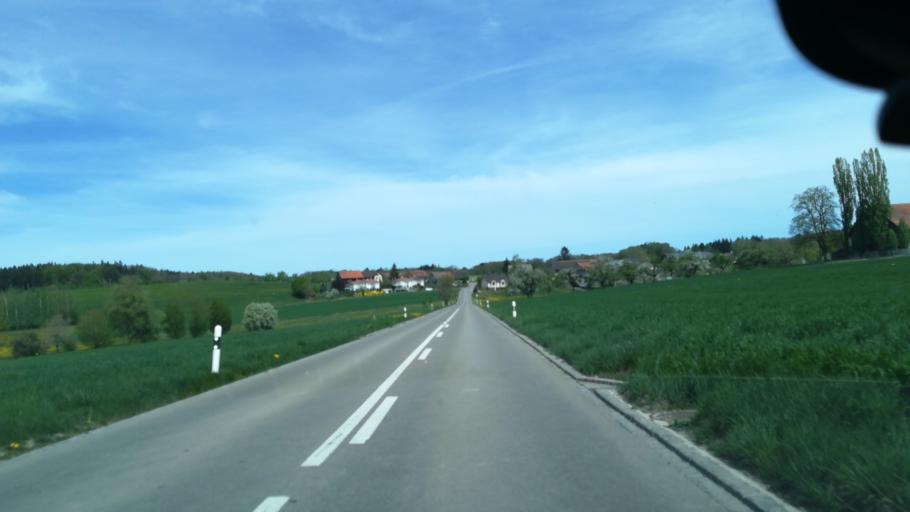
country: CH
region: Thurgau
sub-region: Kreuzlingen District
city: Ermatingen
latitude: 47.6372
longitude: 9.0673
